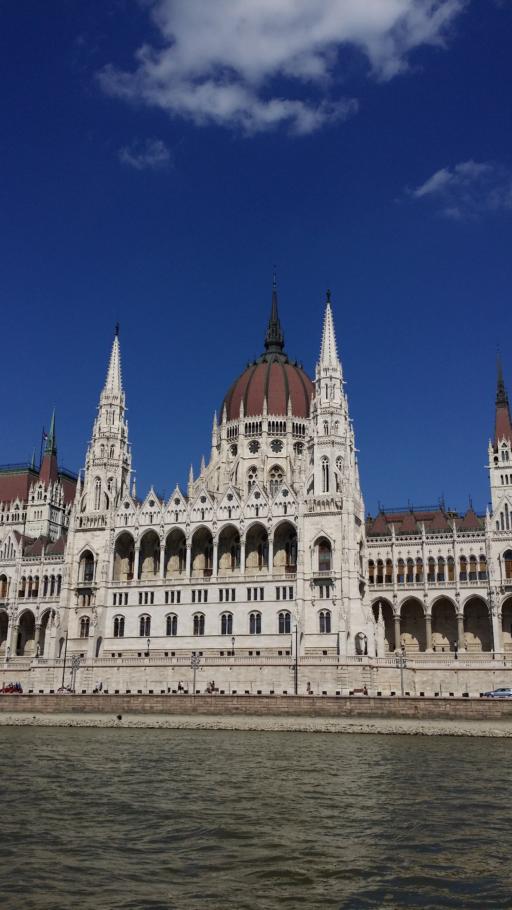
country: HU
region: Budapest
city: Budapest
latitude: 47.5068
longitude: 19.0433
